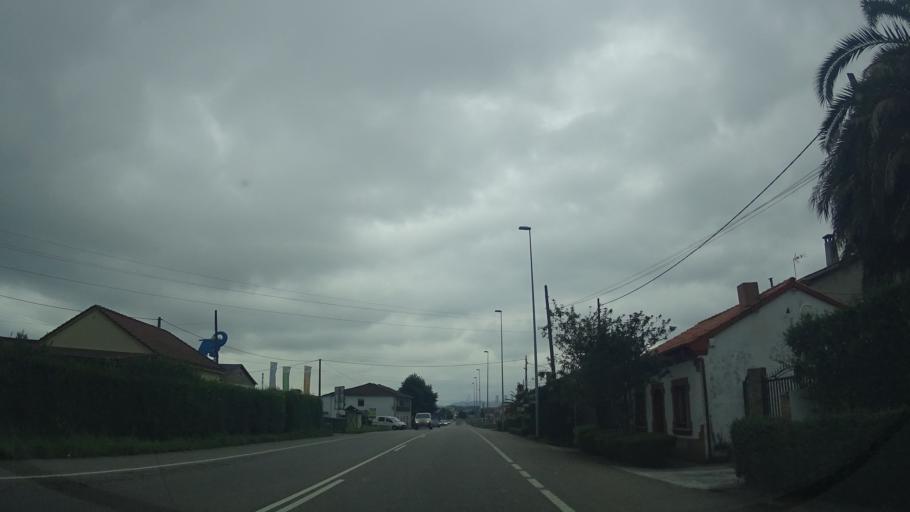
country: ES
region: Asturias
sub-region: Province of Asturias
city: Lugones
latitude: 43.3837
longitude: -5.7640
